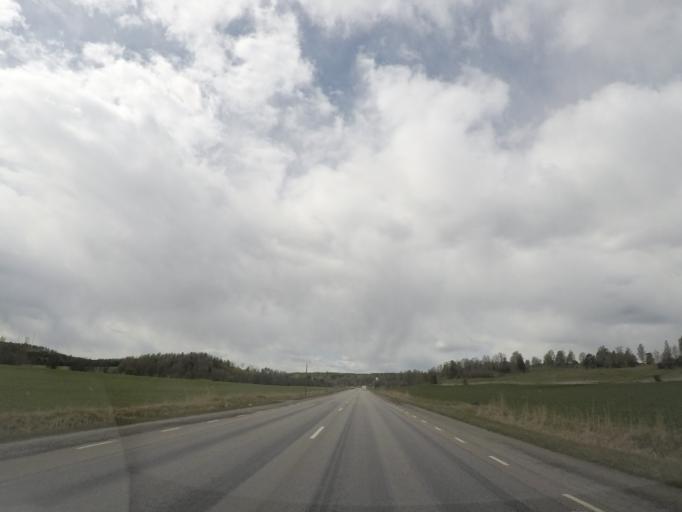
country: SE
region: Soedermanland
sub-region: Nykopings Kommun
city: Olstorp
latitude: 58.7438
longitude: 16.5690
